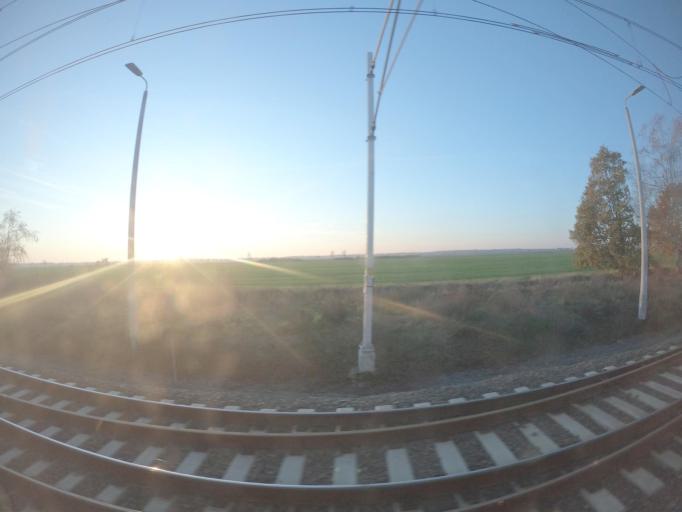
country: PL
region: Lubusz
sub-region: Powiat slubicki
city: Gorzyca
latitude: 52.5238
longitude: 14.6506
